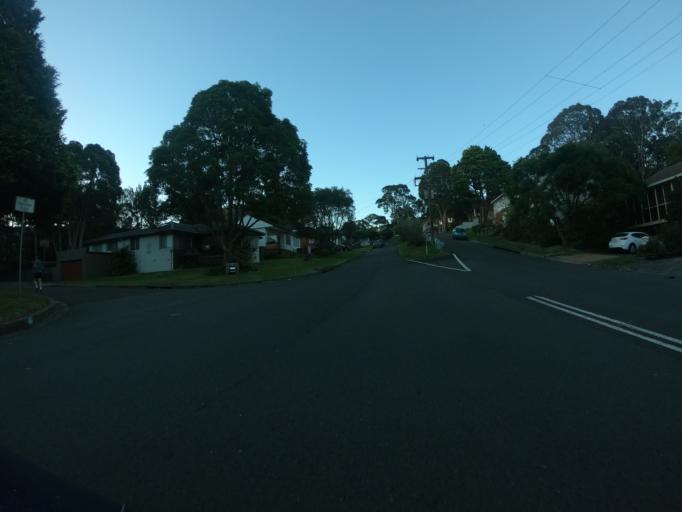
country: AU
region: New South Wales
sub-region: Wollongong
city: Mount Keira
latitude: -34.4211
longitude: 150.8588
